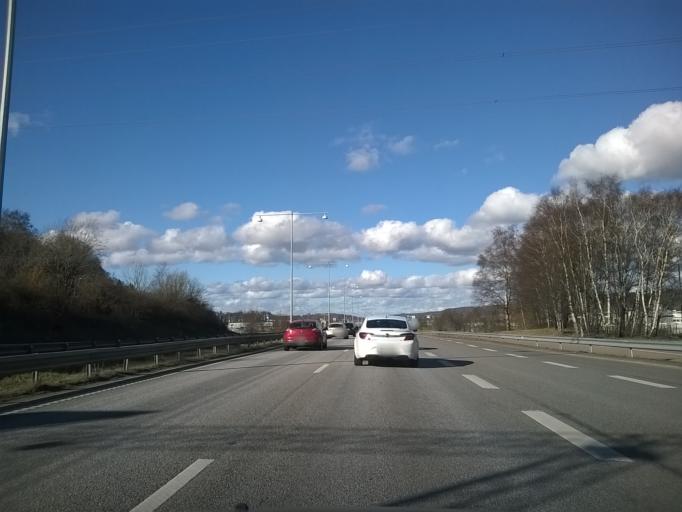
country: SE
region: Vaestra Goetaland
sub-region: Goteborg
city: Hammarkullen
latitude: 57.7621
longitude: 11.9930
